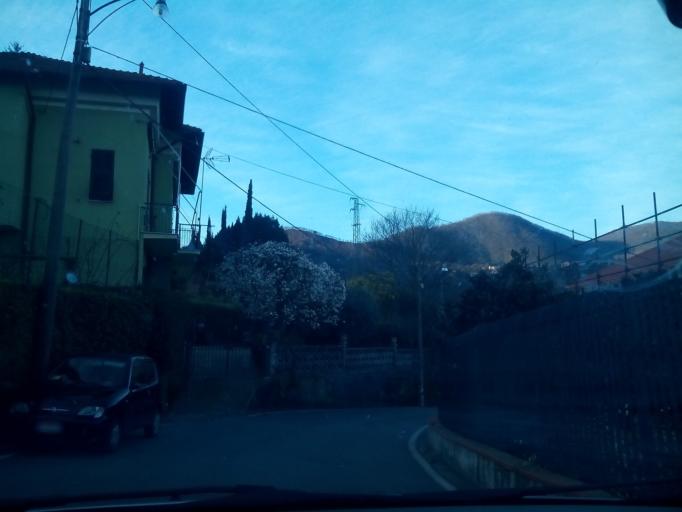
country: IT
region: Liguria
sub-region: Provincia di Genova
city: Davagna
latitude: 44.4441
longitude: 9.0230
